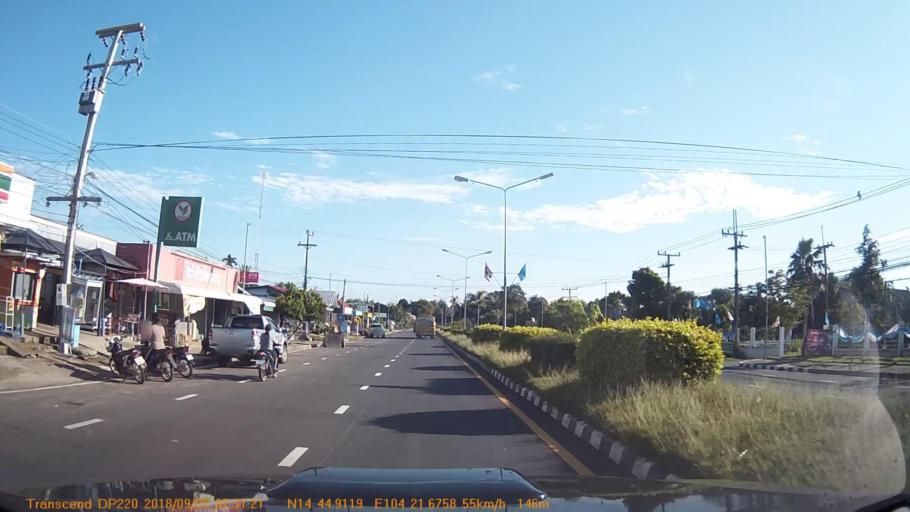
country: TH
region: Sisaket
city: Phrai Bueng
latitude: 14.7489
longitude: 104.3614
